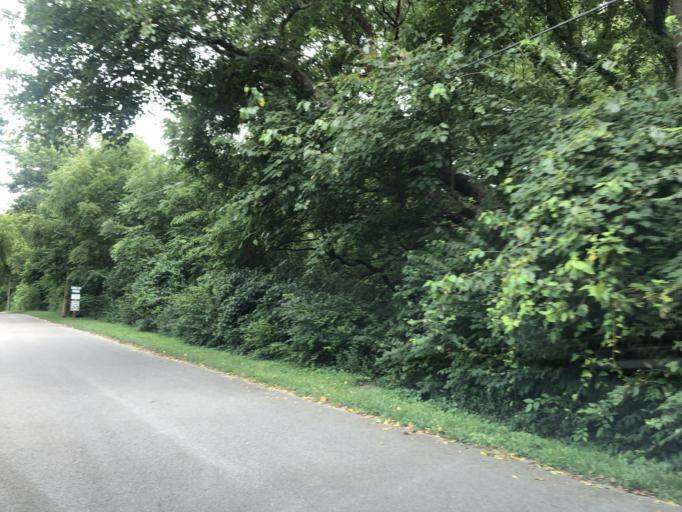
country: US
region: Tennessee
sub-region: Davidson County
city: Nashville
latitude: 36.1660
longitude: -86.7380
